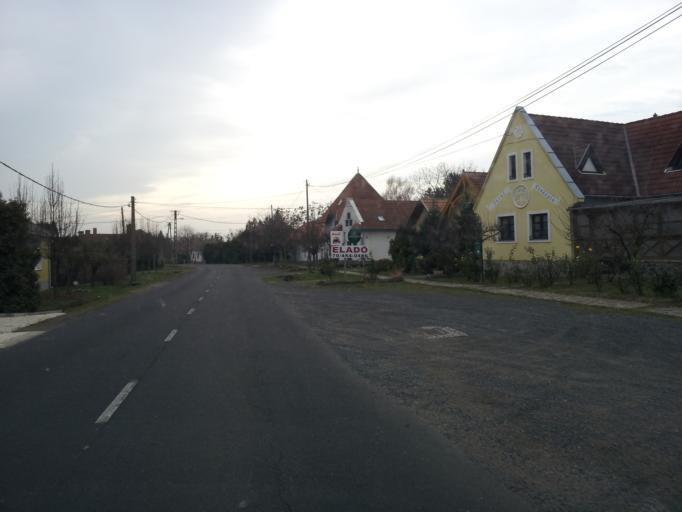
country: HU
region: Zala
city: Cserszegtomaj
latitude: 46.8928
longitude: 17.2296
